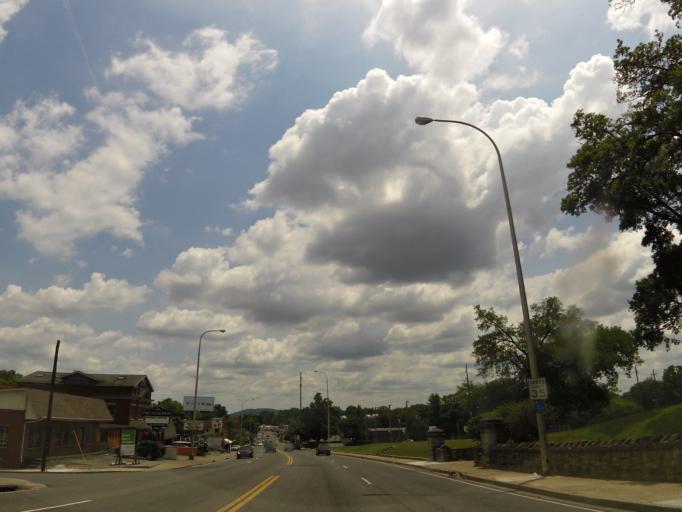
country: US
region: Tennessee
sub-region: Davidson County
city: Nashville
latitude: 36.1379
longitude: -86.7787
